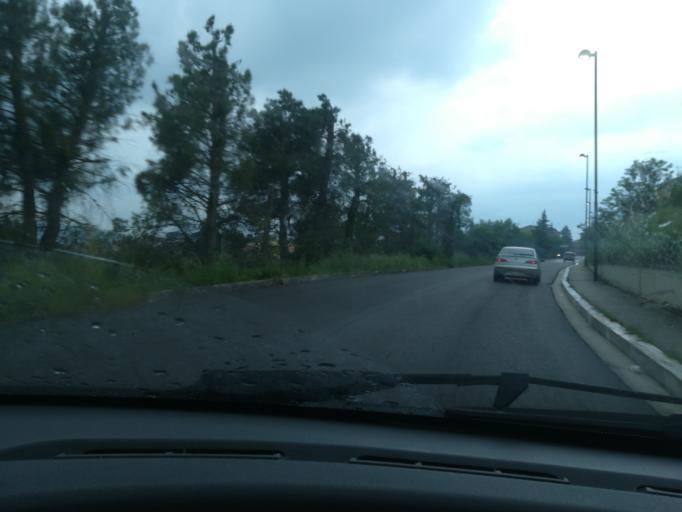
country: IT
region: The Marches
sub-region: Provincia di Macerata
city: Treia
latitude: 43.3097
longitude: 13.3103
